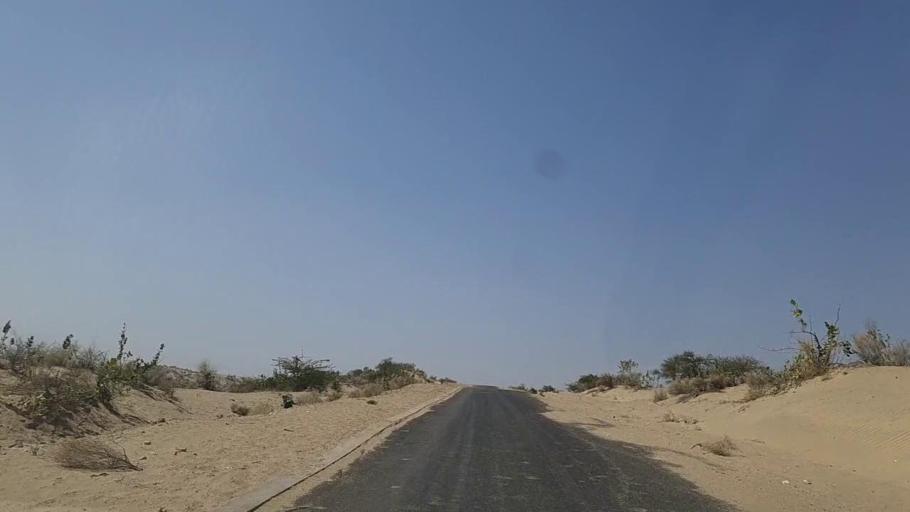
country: PK
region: Sindh
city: Diplo
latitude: 24.5586
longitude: 69.4538
